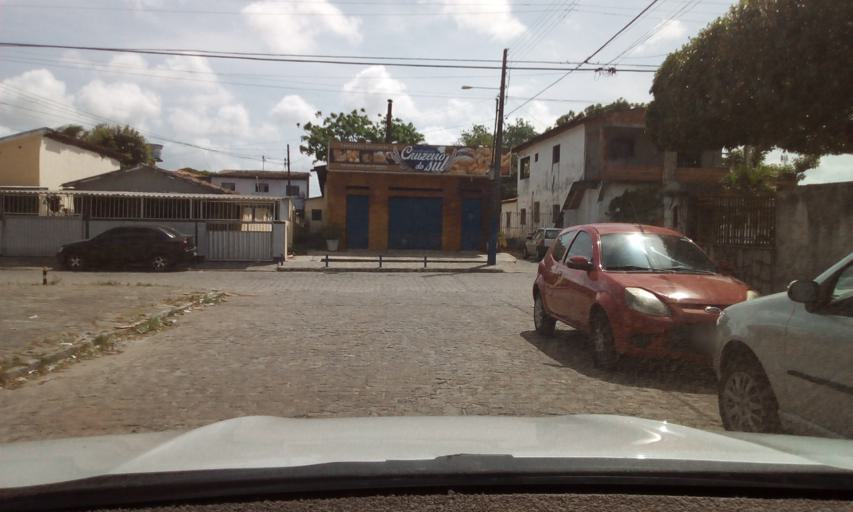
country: BR
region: Paraiba
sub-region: Joao Pessoa
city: Joao Pessoa
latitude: -7.1482
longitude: -34.8915
